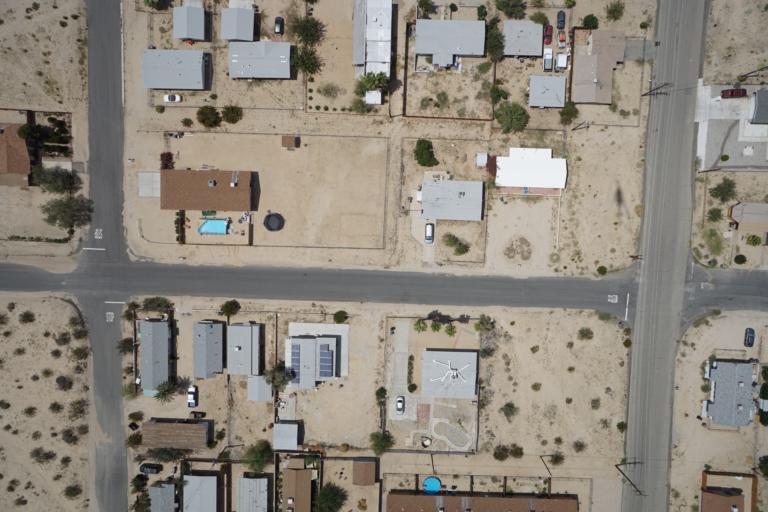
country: US
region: California
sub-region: San Bernardino County
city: Twentynine Palms
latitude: 34.1371
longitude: -116.0487
